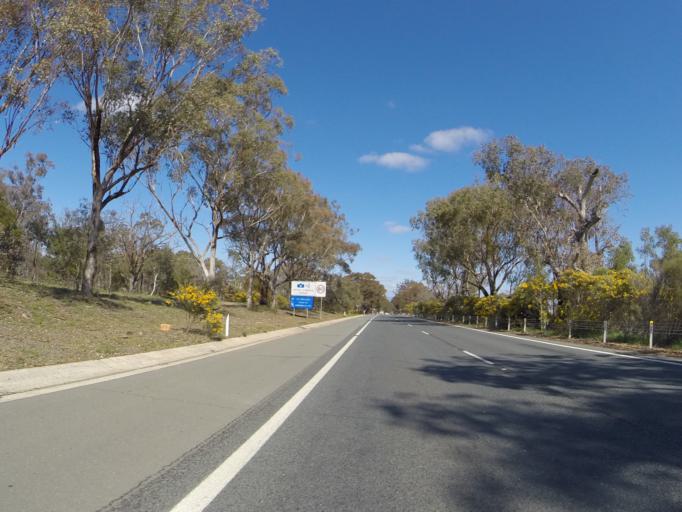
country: AU
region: Australian Capital Territory
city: Kaleen
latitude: -35.2223
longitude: 149.1732
